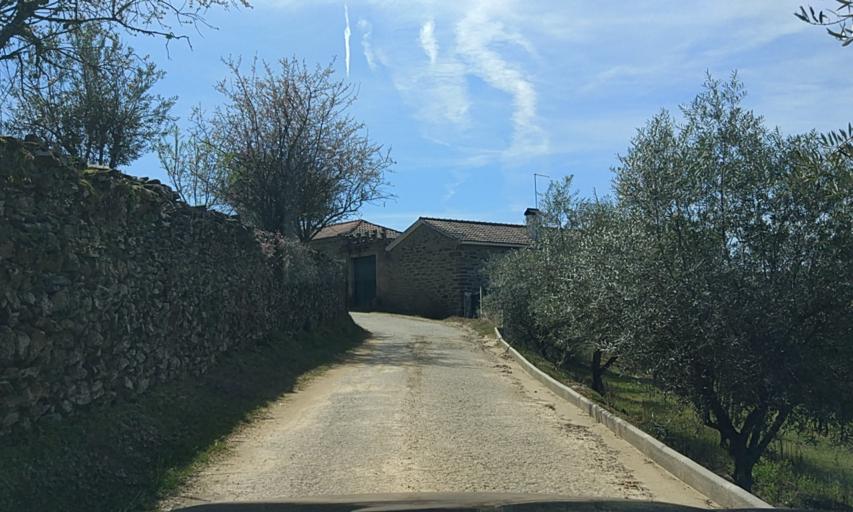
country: PT
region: Vila Real
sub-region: Sabrosa
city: Sabrosa
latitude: 41.3015
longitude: -7.5466
